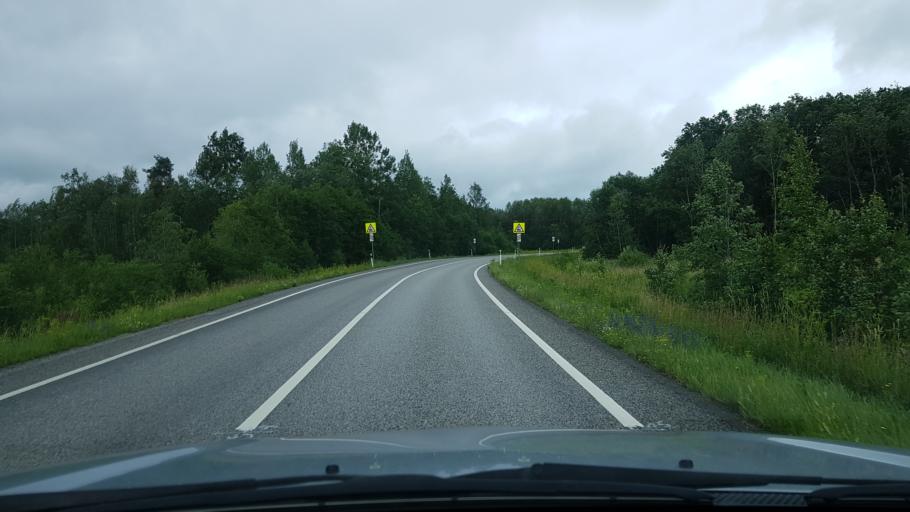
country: EE
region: Ida-Virumaa
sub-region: Narva-Joesuu linn
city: Narva-Joesuu
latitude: 59.3657
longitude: 27.9316
